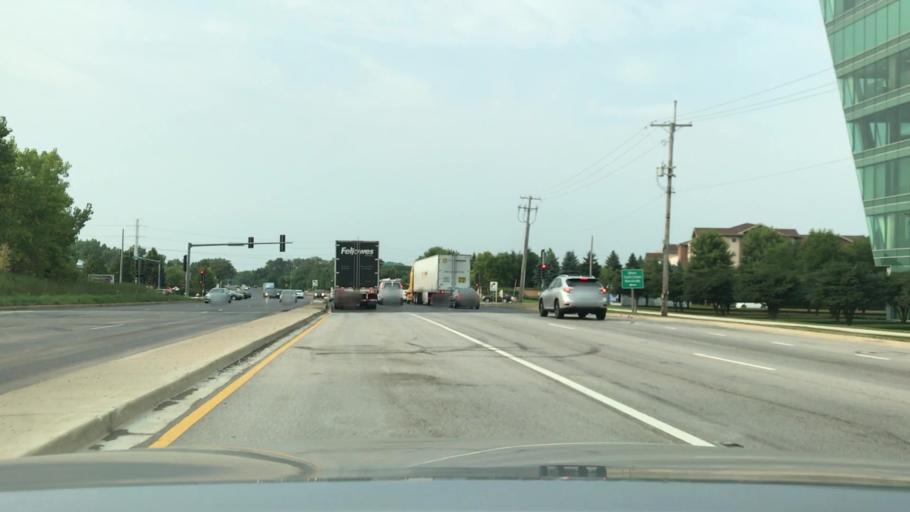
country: US
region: Illinois
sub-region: DuPage County
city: Warrenville
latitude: 41.8087
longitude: -88.2036
